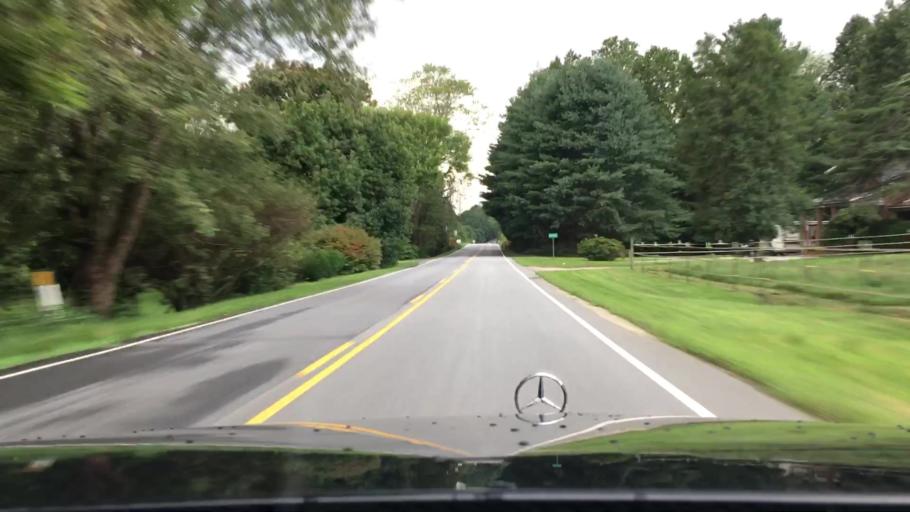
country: US
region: Virginia
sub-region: Nelson County
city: Lovingston
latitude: 37.8002
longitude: -78.9580
